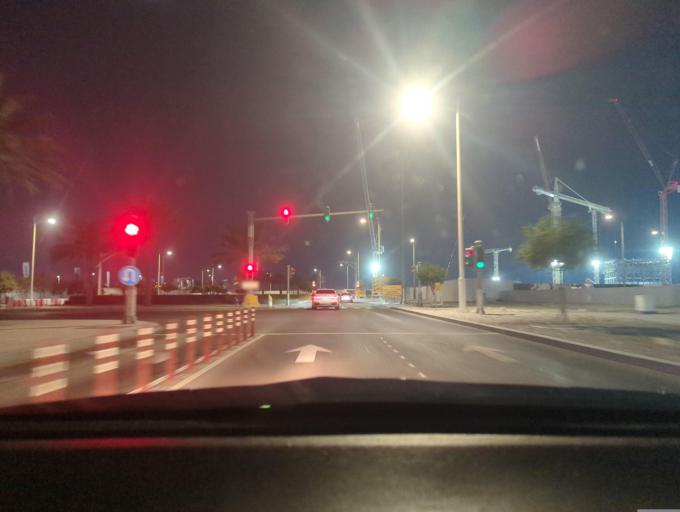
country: AE
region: Abu Dhabi
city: Abu Dhabi
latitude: 24.5378
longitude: 54.4026
